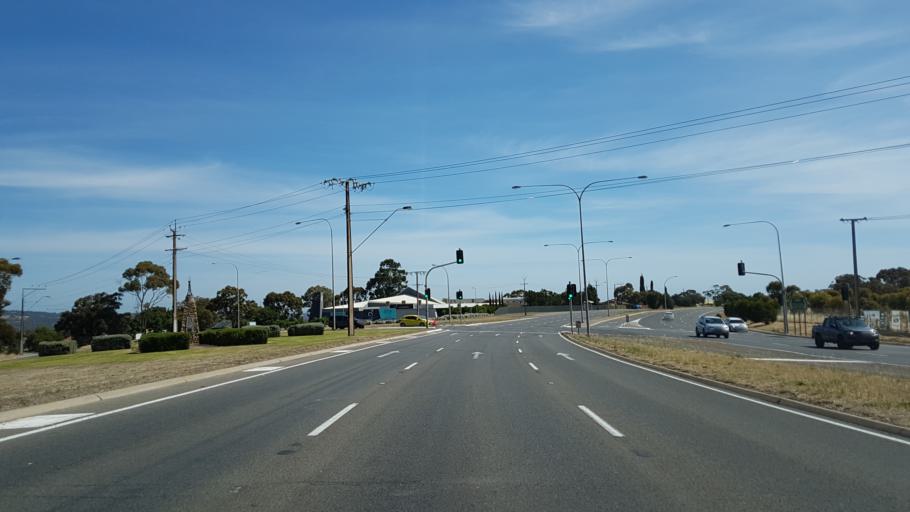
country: AU
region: South Australia
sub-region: Marion
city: Trott Park
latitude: -35.0599
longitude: 138.5598
